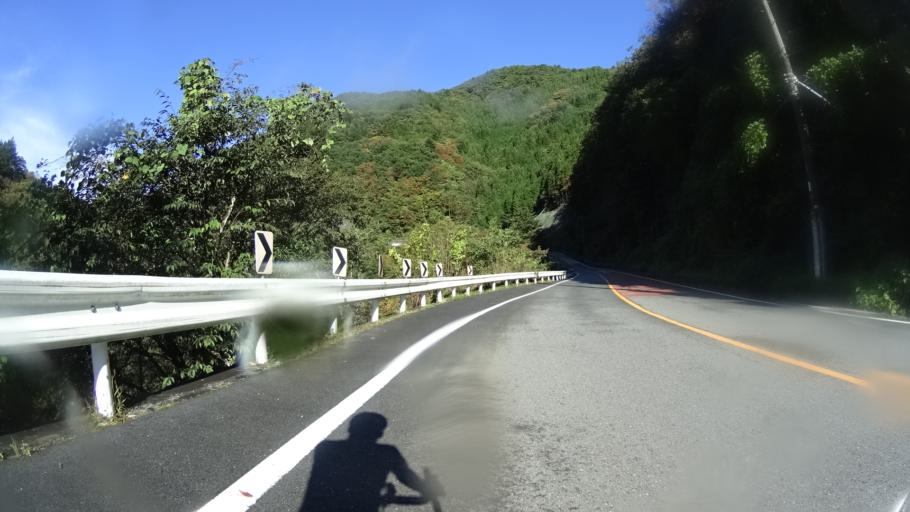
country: JP
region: Yamanashi
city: Otsuki
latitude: 35.7857
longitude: 138.9575
